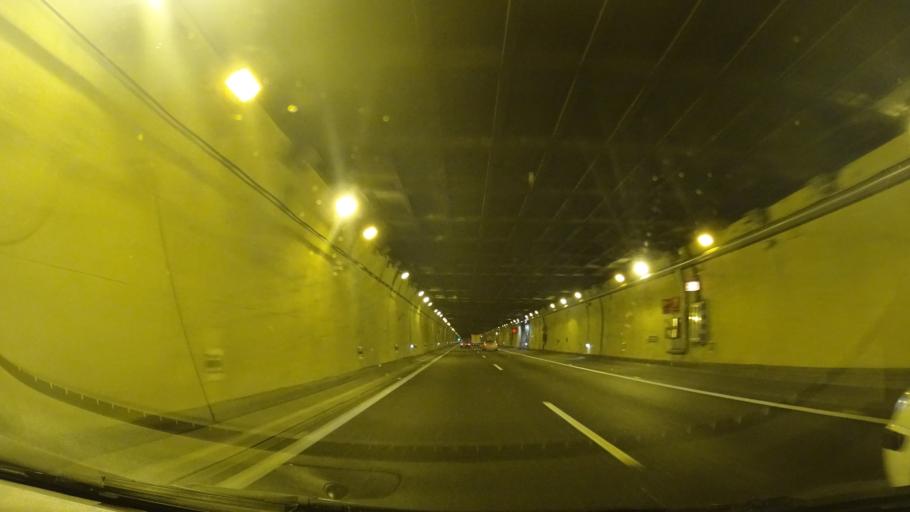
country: ES
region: Madrid
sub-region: Provincia de Madrid
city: Guadarrama
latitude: 40.7032
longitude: -4.1320
